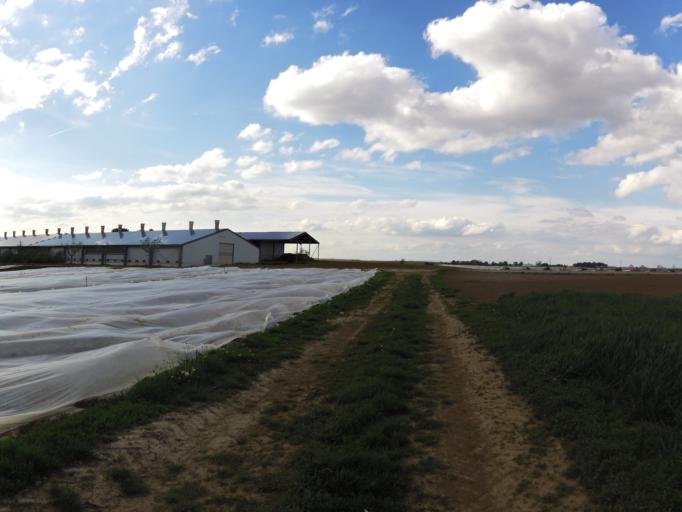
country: DE
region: Bavaria
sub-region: Regierungsbezirk Unterfranken
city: Unterpleichfeld
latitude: 49.8619
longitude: 10.0652
